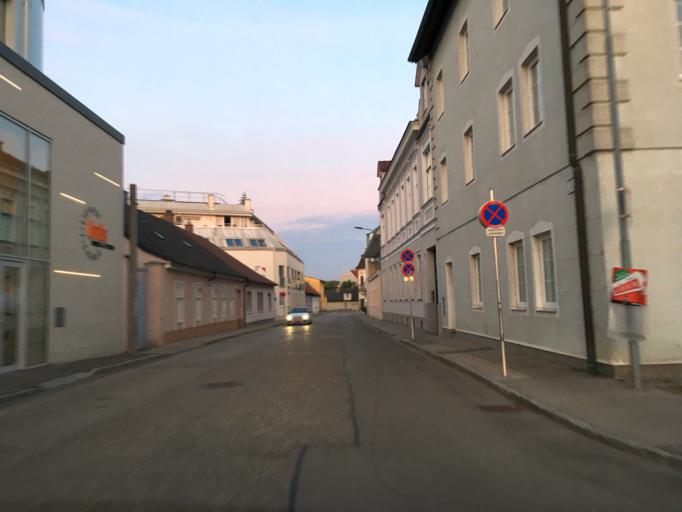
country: AT
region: Lower Austria
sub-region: Politischer Bezirk Korneuburg
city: Stockerau
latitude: 48.3885
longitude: 16.2083
